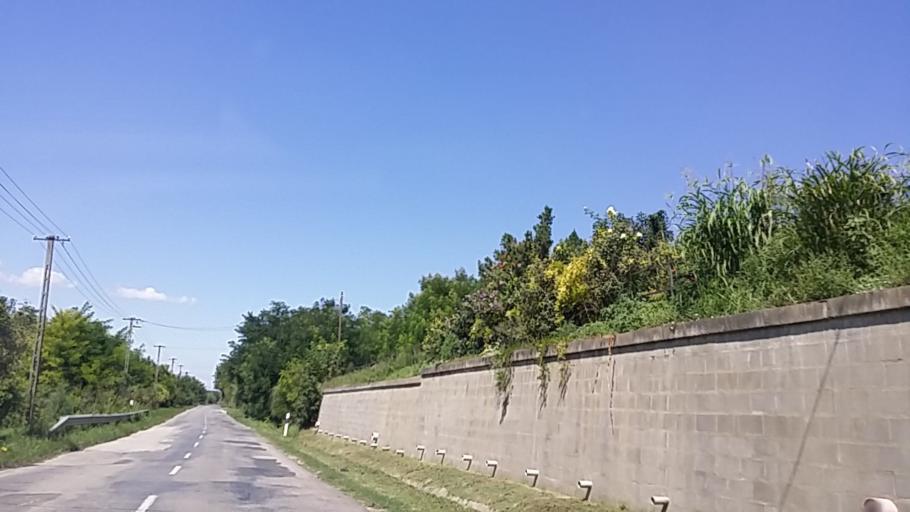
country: HU
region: Tolna
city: Ozora
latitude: 46.7501
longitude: 18.4445
